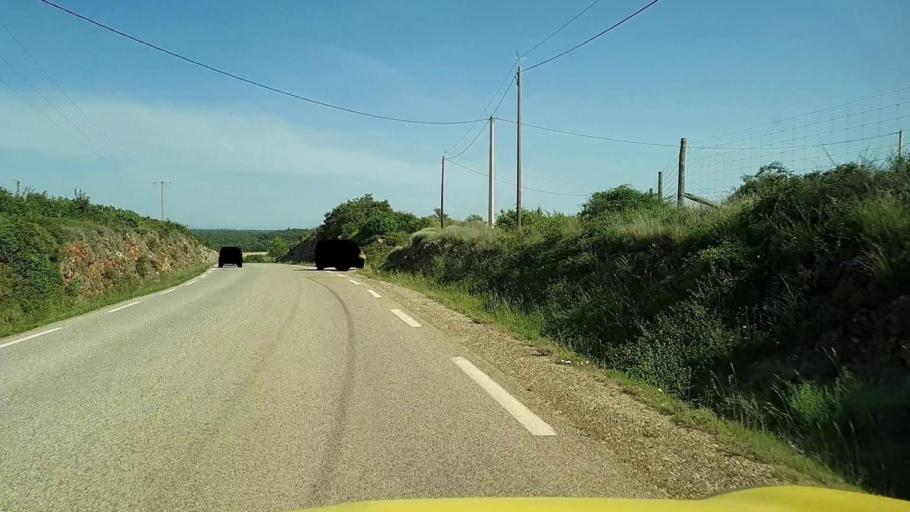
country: FR
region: Languedoc-Roussillon
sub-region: Departement du Gard
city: Montaren-et-Saint-Mediers
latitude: 44.1235
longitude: 4.3670
